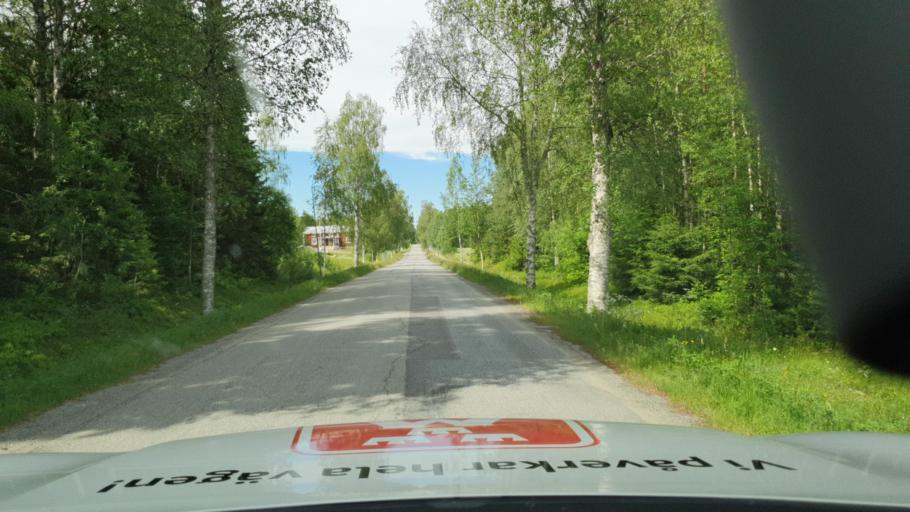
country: SE
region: Vaesterbotten
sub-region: Skelleftea Kommun
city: Burtraesk
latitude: 64.4201
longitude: 20.5440
